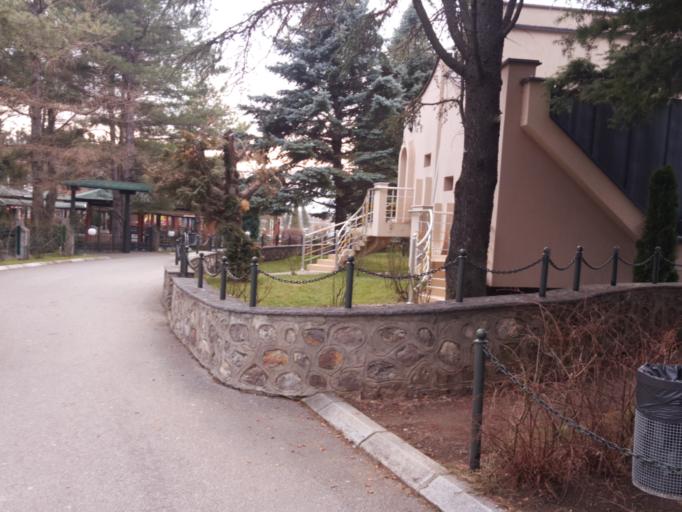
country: XK
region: Pec
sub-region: Komuna e Istogut
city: Istok
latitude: 42.7802
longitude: 20.4825
